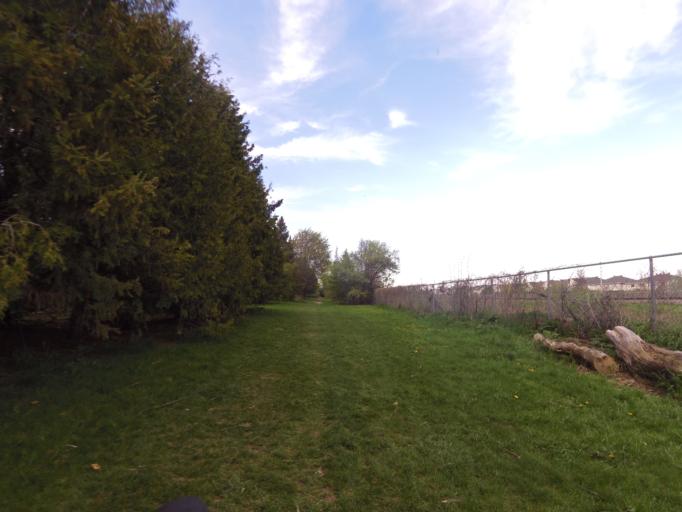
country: CA
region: Ontario
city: Bells Corners
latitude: 45.2891
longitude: -75.7449
